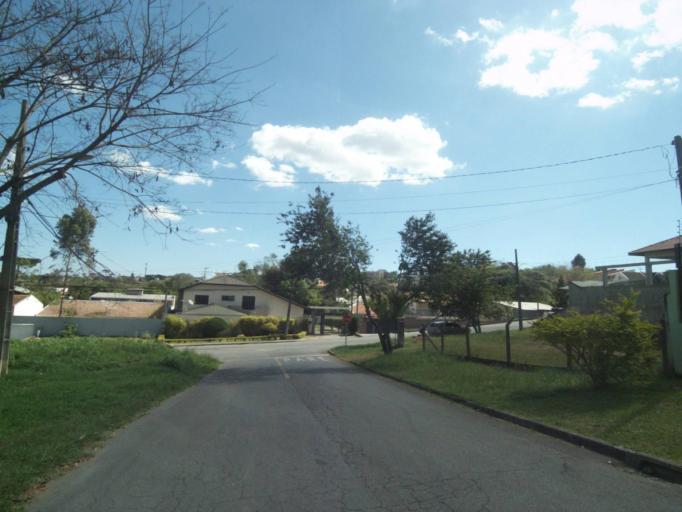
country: BR
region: Parana
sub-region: Curitiba
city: Curitiba
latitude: -25.3765
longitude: -49.2479
